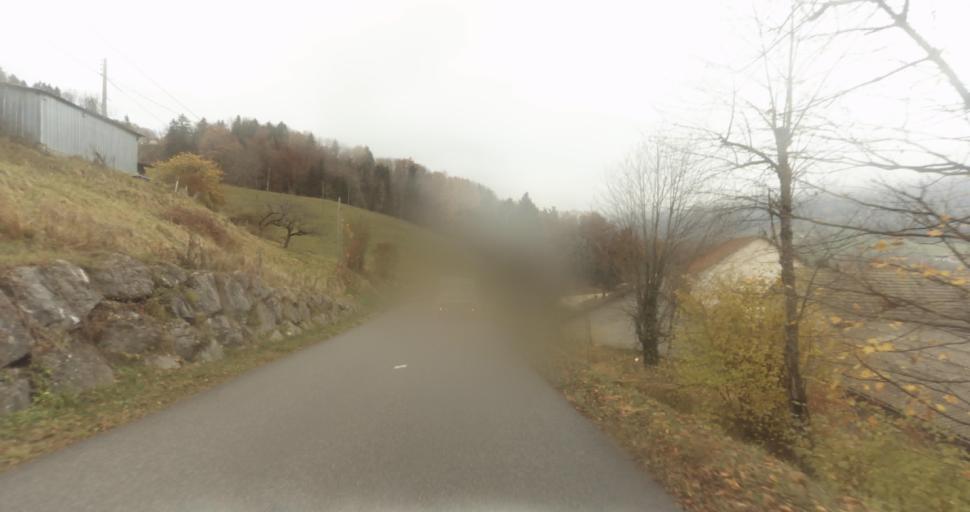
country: FR
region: Rhone-Alpes
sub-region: Departement de la Haute-Savoie
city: Thorens-Glieres
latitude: 46.0030
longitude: 6.2495
